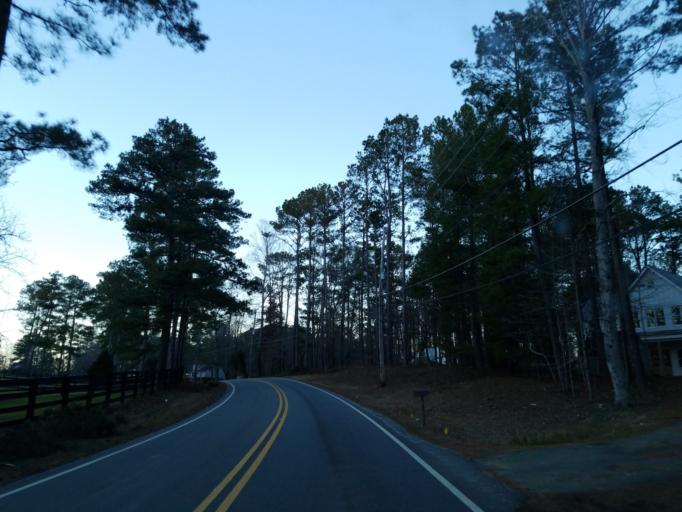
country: US
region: Georgia
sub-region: Cherokee County
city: Holly Springs
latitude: 34.1235
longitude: -84.4227
